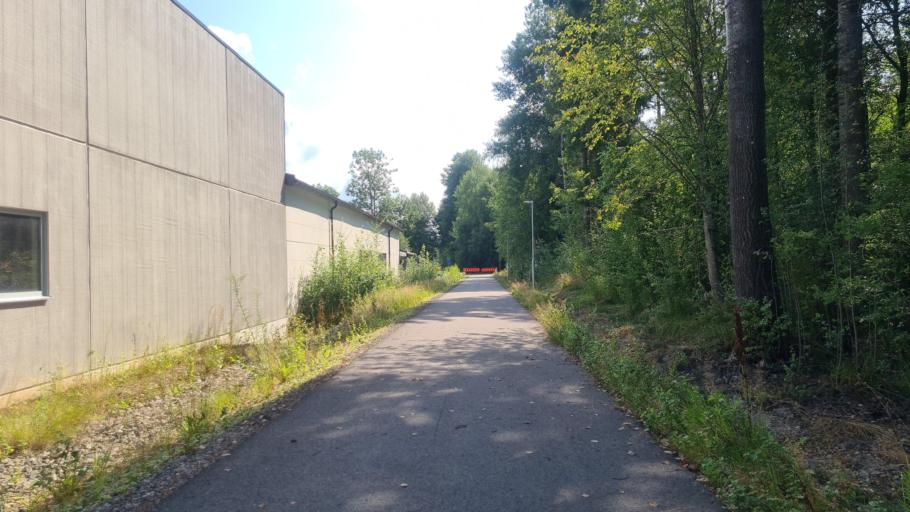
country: SE
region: Kronoberg
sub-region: Ljungby Kommun
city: Ljungby
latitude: 56.8239
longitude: 13.9211
